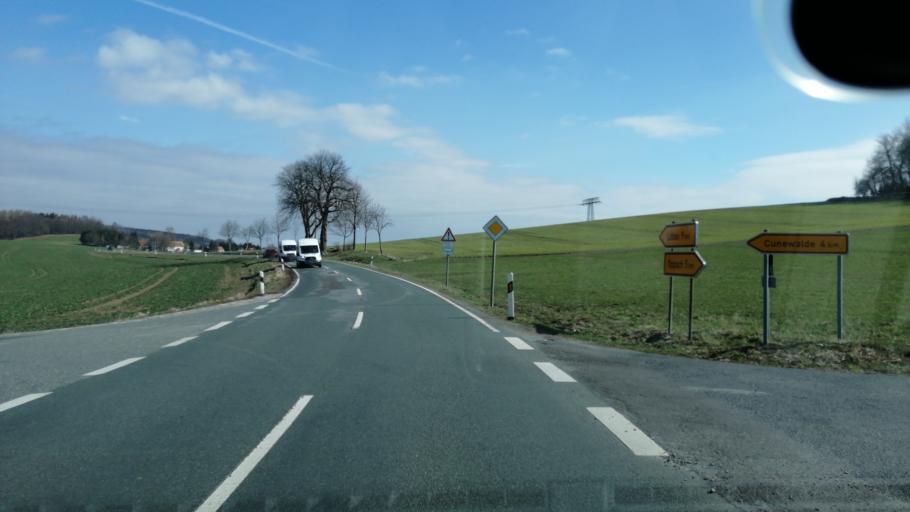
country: DE
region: Saxony
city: Schonbach
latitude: 51.0796
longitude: 14.5579
